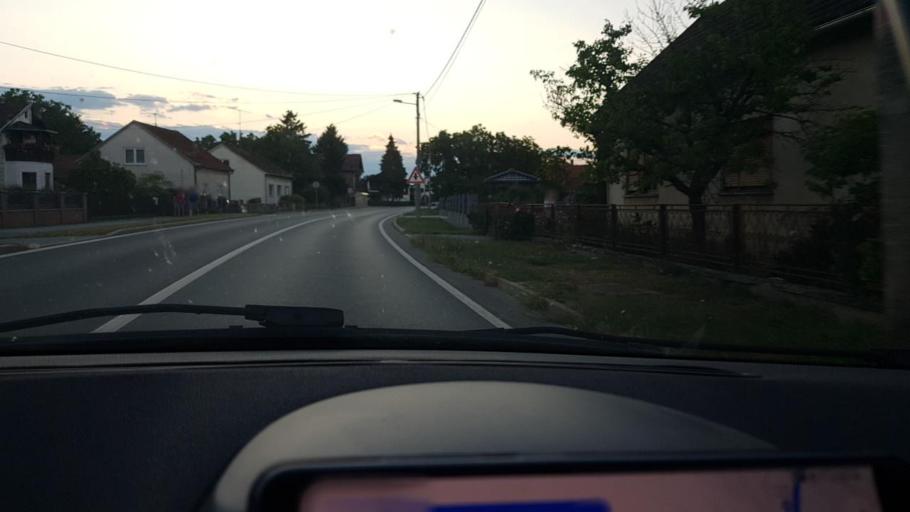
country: HR
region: Bjelovarsko-Bilogorska
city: Zdralovi
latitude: 45.8772
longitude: 16.8737
